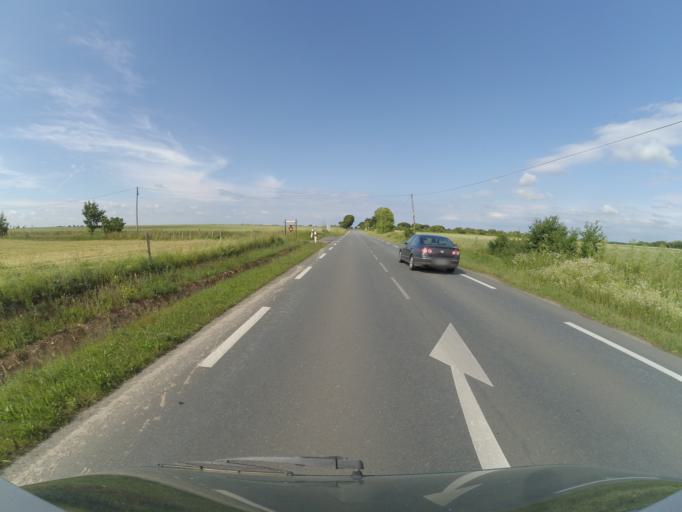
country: FR
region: Poitou-Charentes
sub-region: Departement de la Charente-Maritime
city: Saint-Xandre
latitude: 46.2301
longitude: -1.0783
